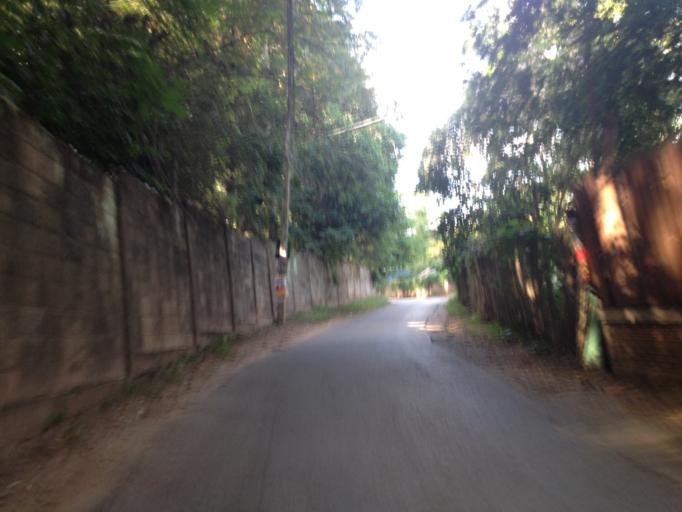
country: TH
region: Chiang Mai
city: Chiang Mai
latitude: 18.7845
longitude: 98.9525
